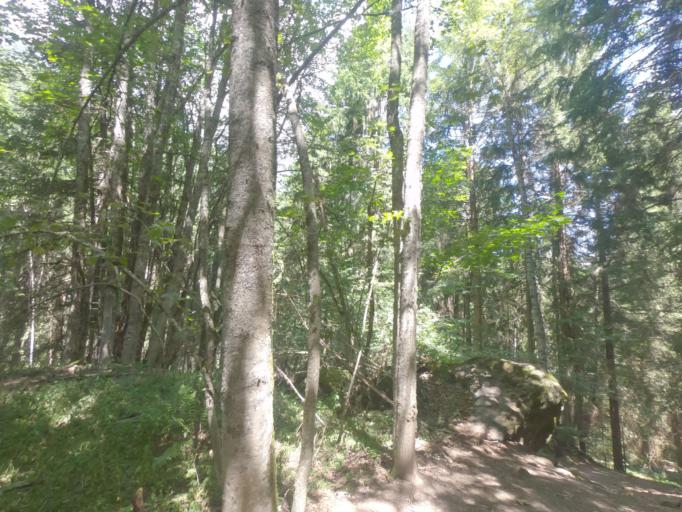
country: CH
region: Valais
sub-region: Saint-Maurice District
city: Salvan
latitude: 46.0716
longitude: 6.9703
